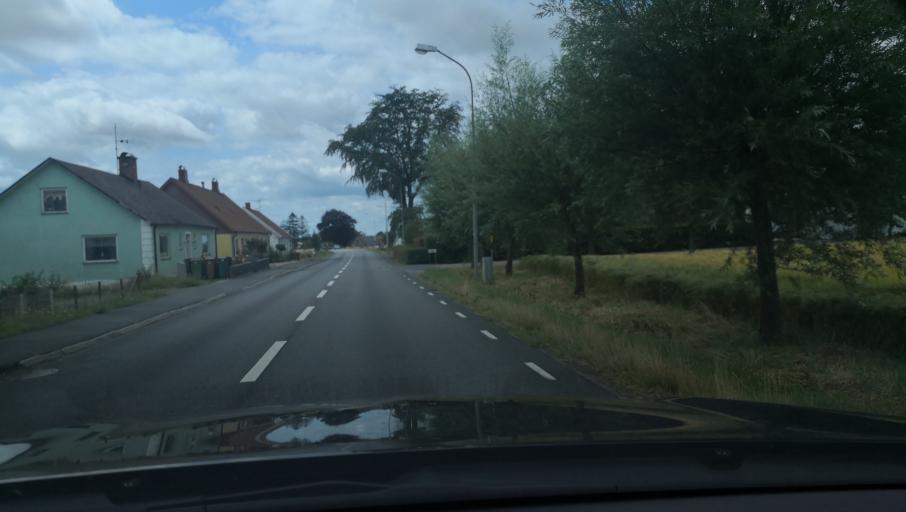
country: SE
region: Skane
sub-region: Tomelilla Kommun
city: Tomelilla
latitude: 55.4986
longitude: 14.1377
